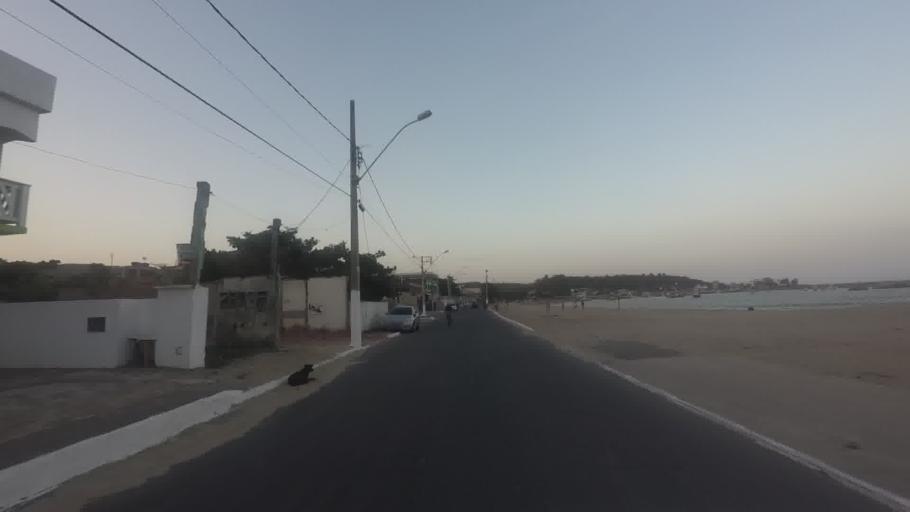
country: BR
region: Espirito Santo
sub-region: Piuma
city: Piuma
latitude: -20.8945
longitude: -40.7745
